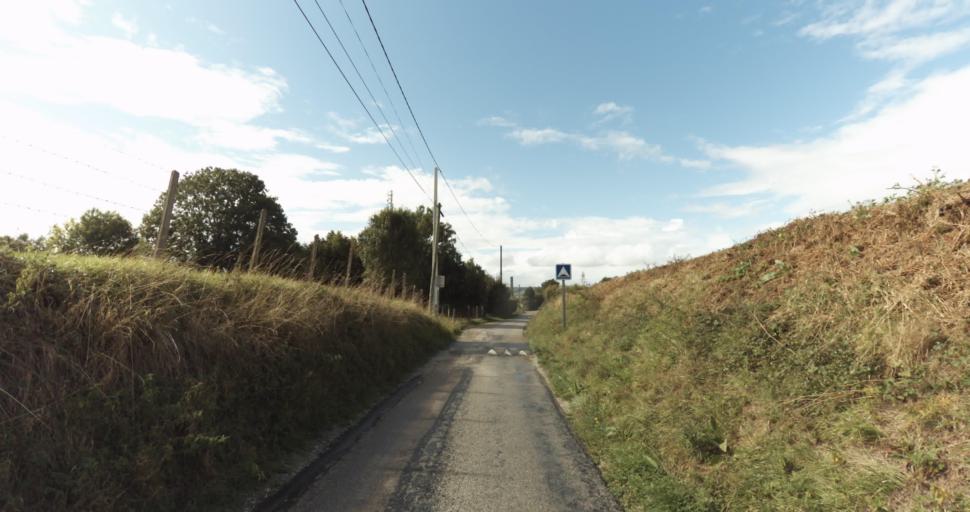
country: FR
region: Lower Normandy
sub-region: Departement de l'Orne
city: Gace
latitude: 48.7902
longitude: 0.3061
